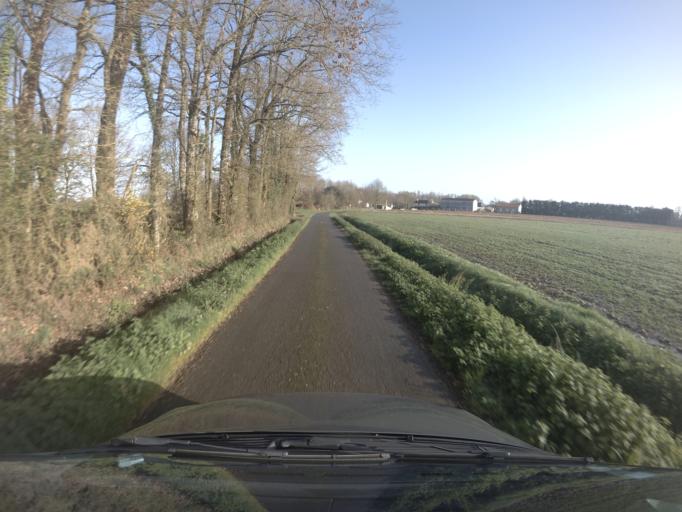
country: FR
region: Pays de la Loire
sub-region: Departement de la Loire-Atlantique
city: La Planche
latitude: 47.0206
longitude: -1.4577
